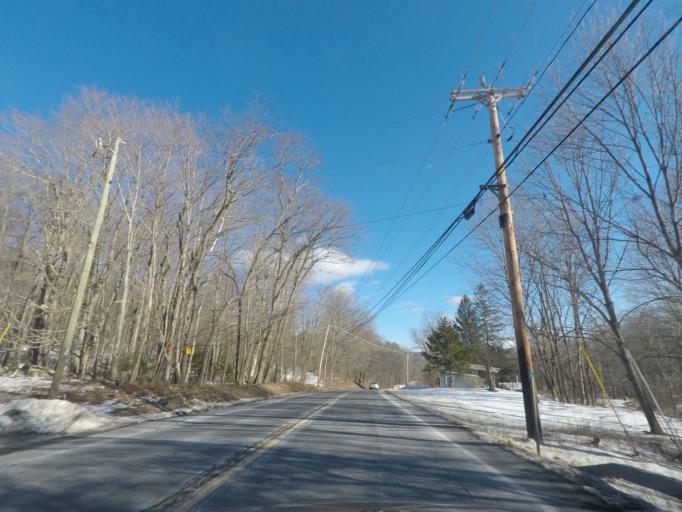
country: US
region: New York
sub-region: Columbia County
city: Chatham
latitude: 42.3189
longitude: -73.4878
